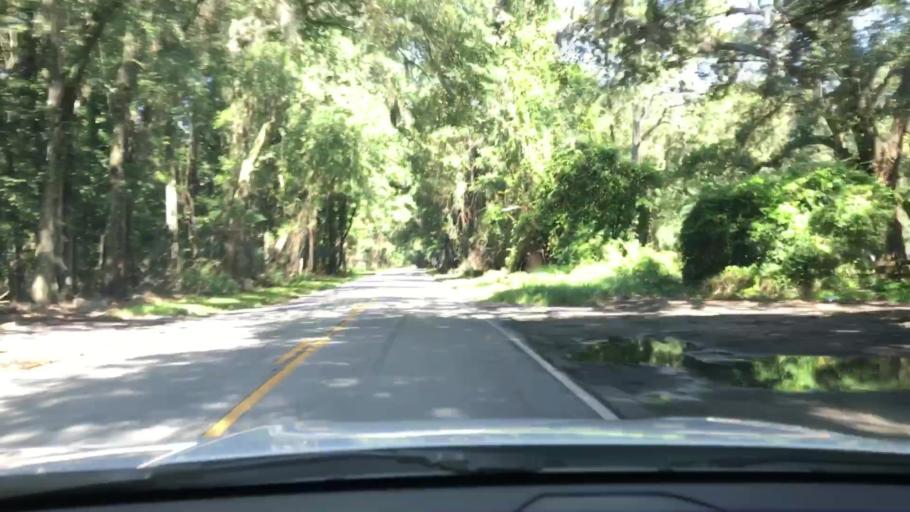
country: US
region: South Carolina
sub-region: Berkeley County
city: Ladson
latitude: 32.8939
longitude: -80.1333
